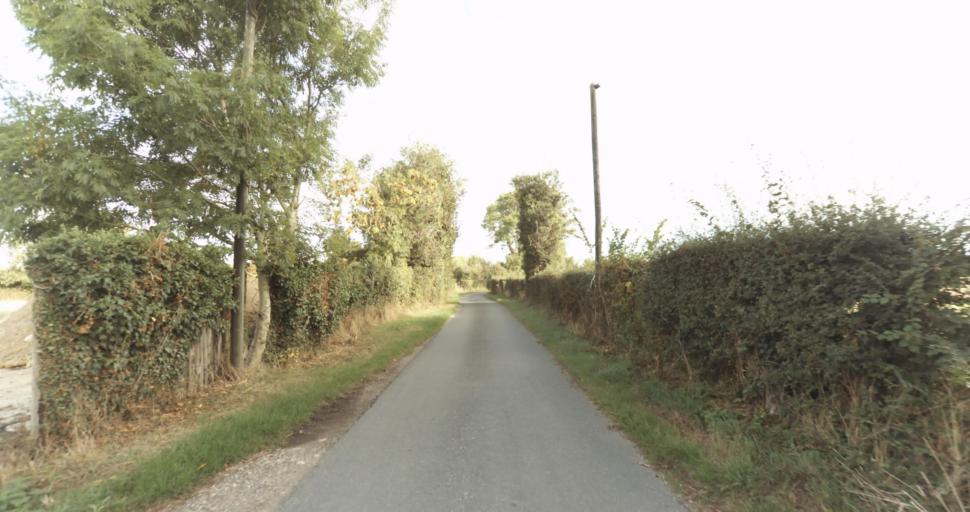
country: FR
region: Lower Normandy
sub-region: Departement de l'Orne
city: Vimoutiers
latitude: 48.8848
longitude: 0.2365
